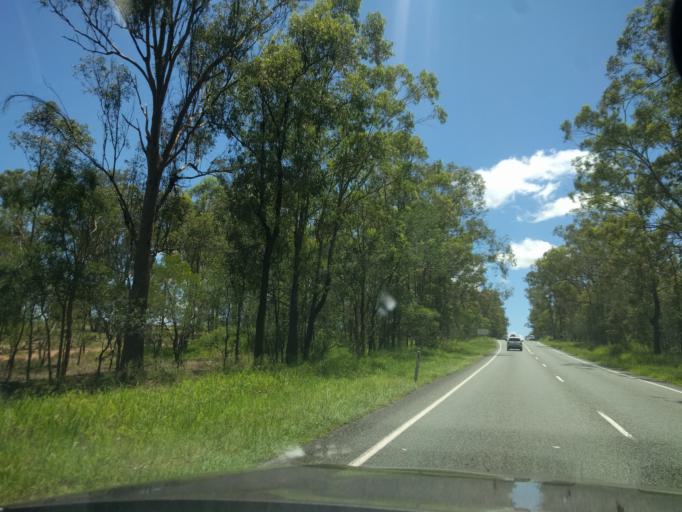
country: AU
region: Queensland
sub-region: Logan
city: Cedar Vale
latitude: -27.8556
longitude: 153.0086
